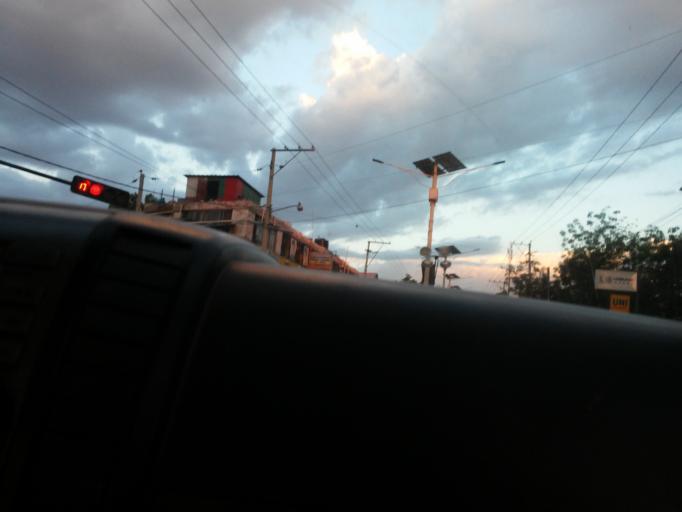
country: HT
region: Ouest
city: Port-au-Prince
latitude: 18.5567
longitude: -72.3248
